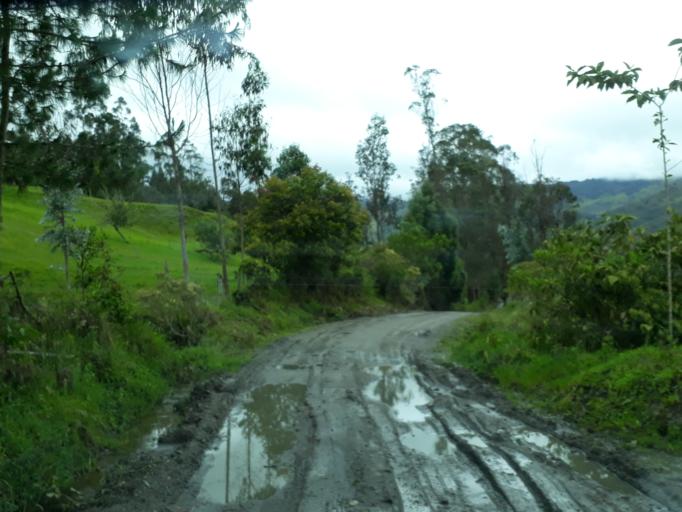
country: CO
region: Cundinamarca
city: Junin
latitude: 4.6511
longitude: -73.6631
